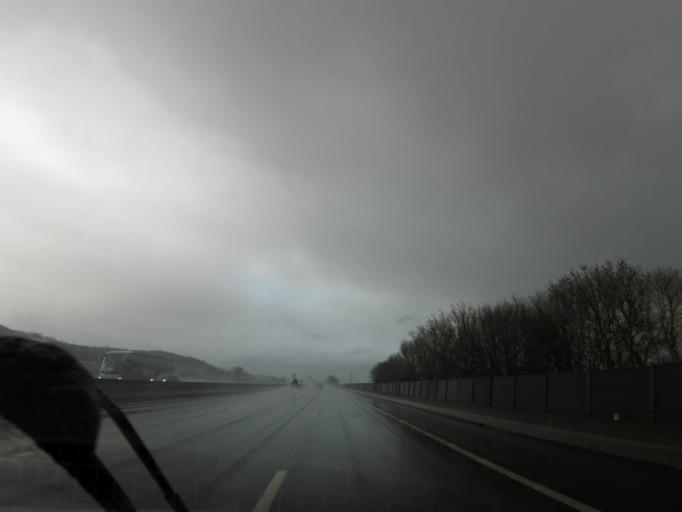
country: FR
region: Bourgogne
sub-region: Departement de Saone-et-Loire
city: Saint-Martin-Belle-Roche
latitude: 46.3817
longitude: 4.8481
